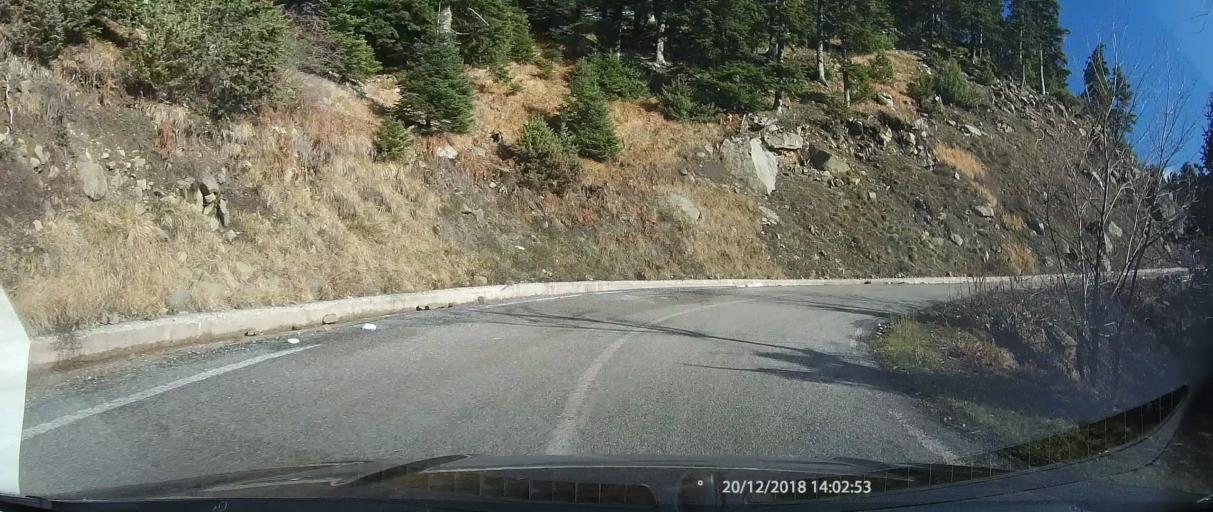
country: GR
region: West Greece
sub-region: Nomos Aitolias kai Akarnanias
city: Thermo
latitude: 38.7384
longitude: 21.6400
